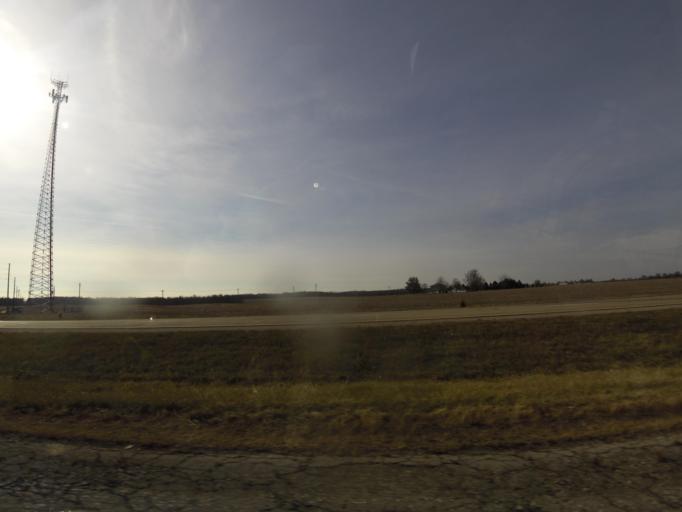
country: US
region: Illinois
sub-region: De Witt County
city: Clinton
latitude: 40.1408
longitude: -88.9797
